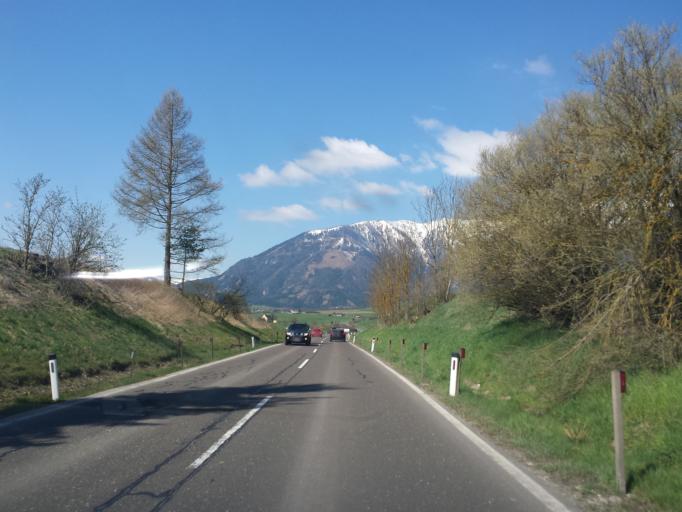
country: AT
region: Styria
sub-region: Politischer Bezirk Leoben
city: Trofaiach
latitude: 47.4073
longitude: 14.9830
